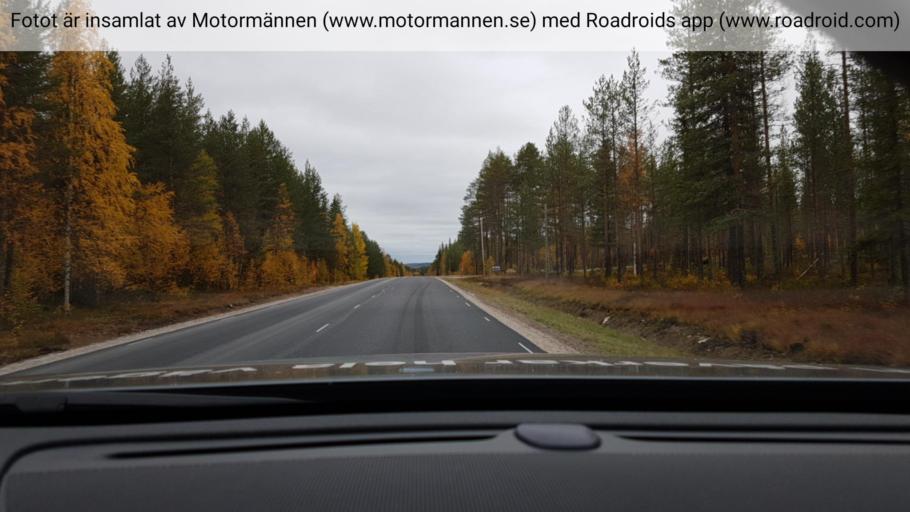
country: SE
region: Norrbotten
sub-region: Overkalix Kommun
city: OEverkalix
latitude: 66.3764
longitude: 22.8382
